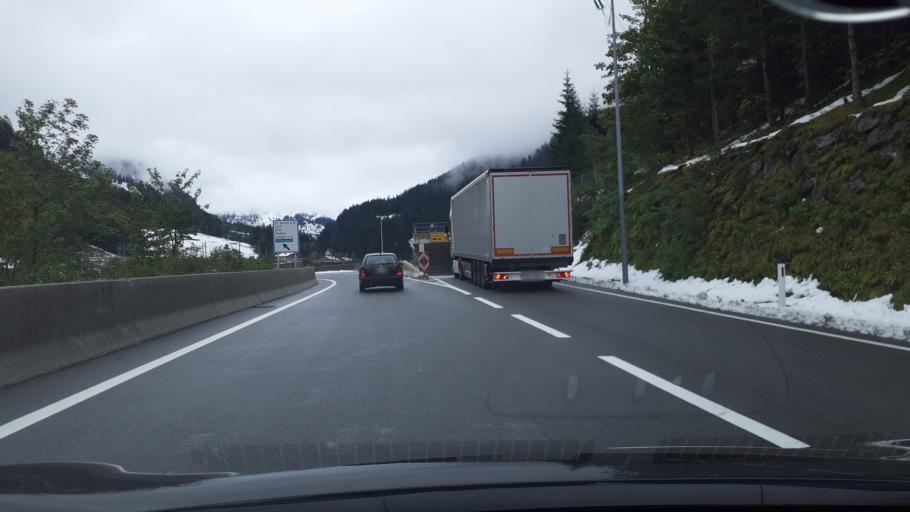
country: AT
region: Vorarlberg
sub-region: Politischer Bezirk Bludenz
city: Klosterle
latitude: 47.1302
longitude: 10.1131
